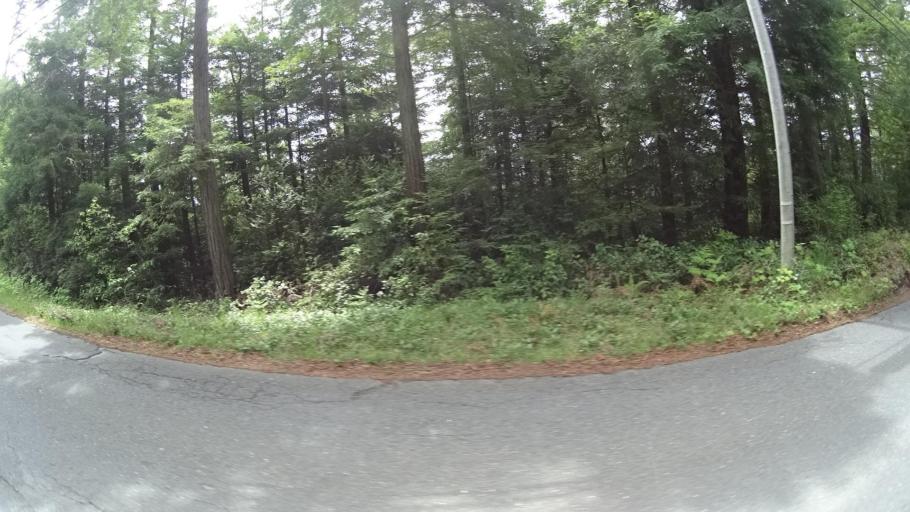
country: US
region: California
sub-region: Humboldt County
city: Bayside
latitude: 40.7871
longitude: -124.0649
